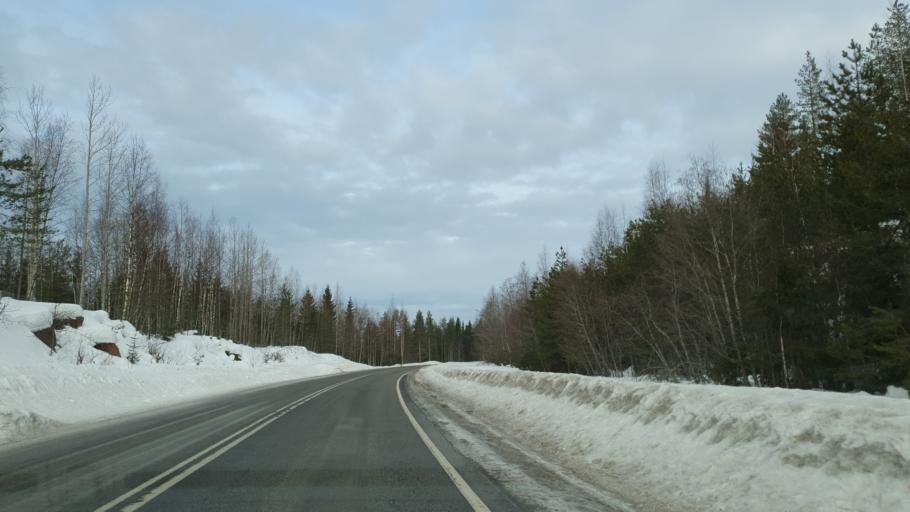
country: FI
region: Kainuu
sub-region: Kajaani
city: Paltamo
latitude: 64.2543
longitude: 28.0341
